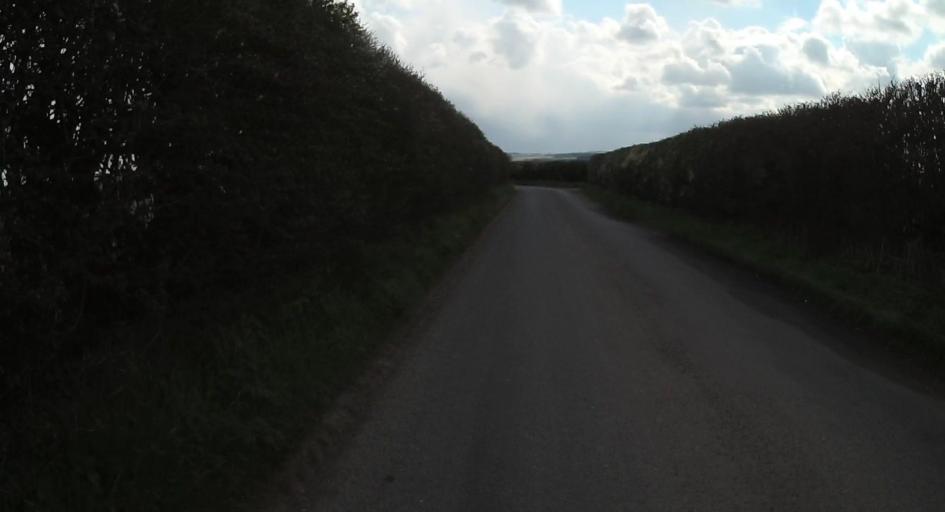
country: GB
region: England
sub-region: Hampshire
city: Kings Worthy
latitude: 51.1005
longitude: -1.2023
